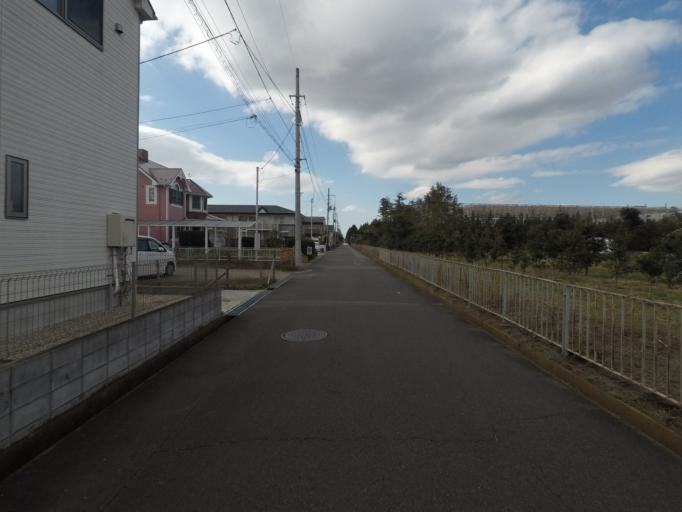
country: JP
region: Ibaraki
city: Ushiku
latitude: 36.0253
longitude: 140.0999
